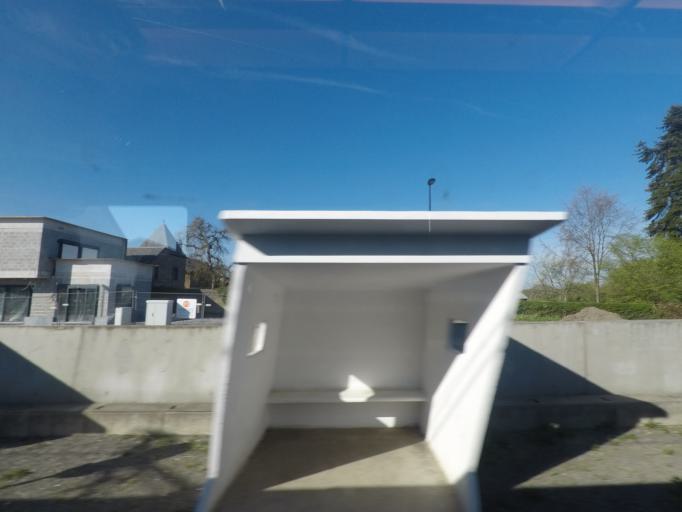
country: BE
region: Wallonia
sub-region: Province de Namur
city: Rochefort
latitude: 50.2492
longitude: 5.1942
